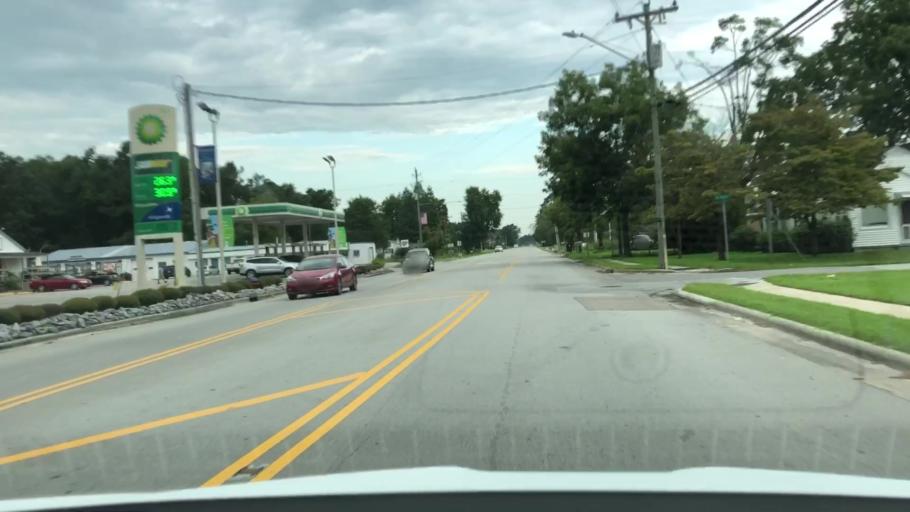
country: US
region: North Carolina
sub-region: Jones County
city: Trenton
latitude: 35.0659
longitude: -77.3603
